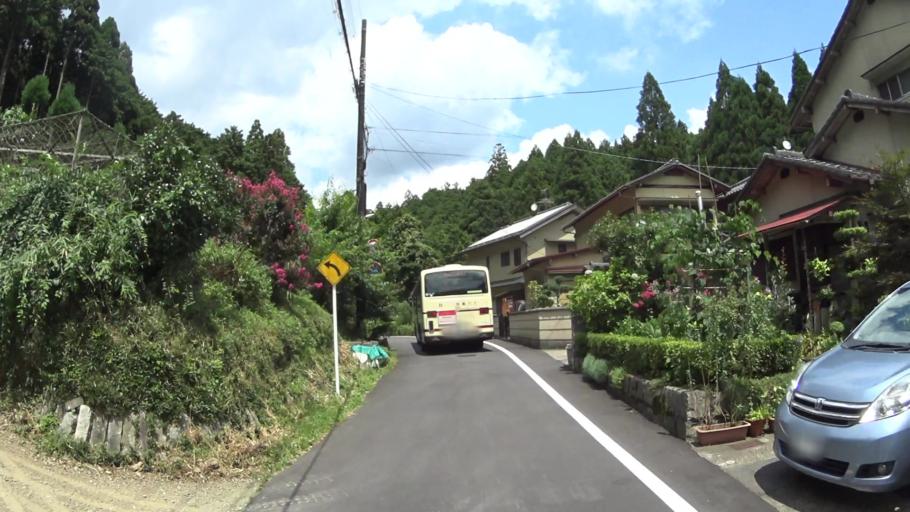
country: JP
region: Shiga Prefecture
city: Kitahama
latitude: 35.1268
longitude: 135.8322
